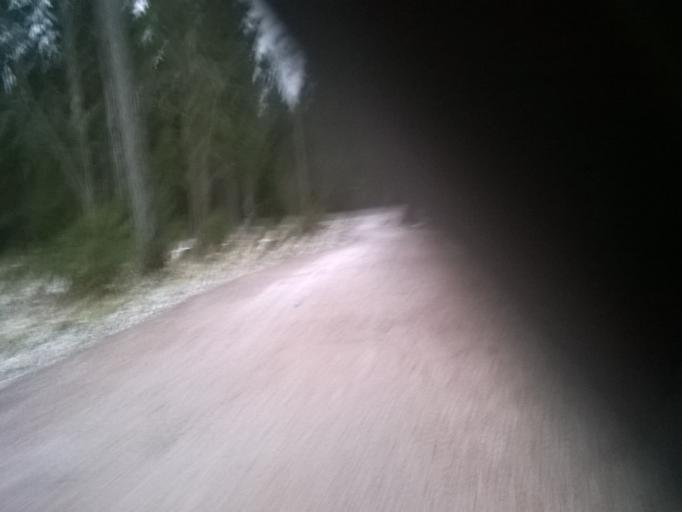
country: FI
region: Uusimaa
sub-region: Helsinki
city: Helsinki
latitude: 60.2541
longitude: 24.9056
